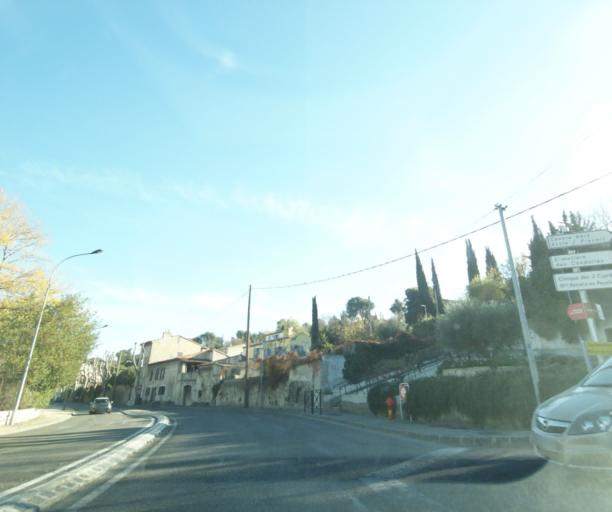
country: FR
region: Provence-Alpes-Cote d'Azur
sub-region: Departement des Bouches-du-Rhone
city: La Penne-sur-Huveaune
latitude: 43.2825
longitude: 5.5078
